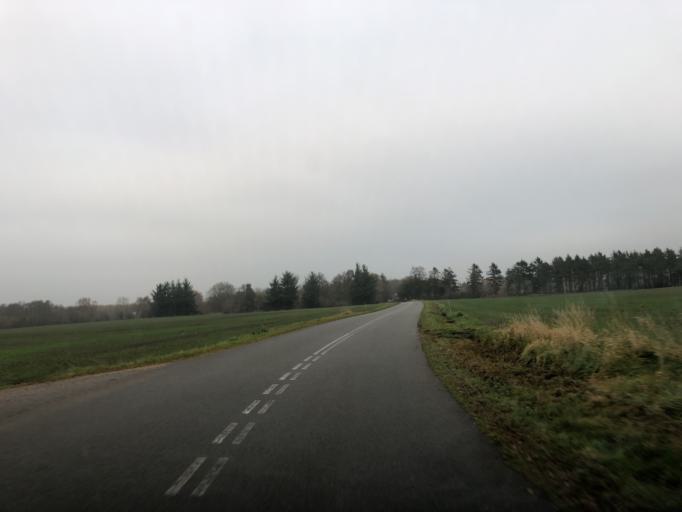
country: DK
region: Central Jutland
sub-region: Herning Kommune
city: Avlum
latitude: 56.2435
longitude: 8.8807
